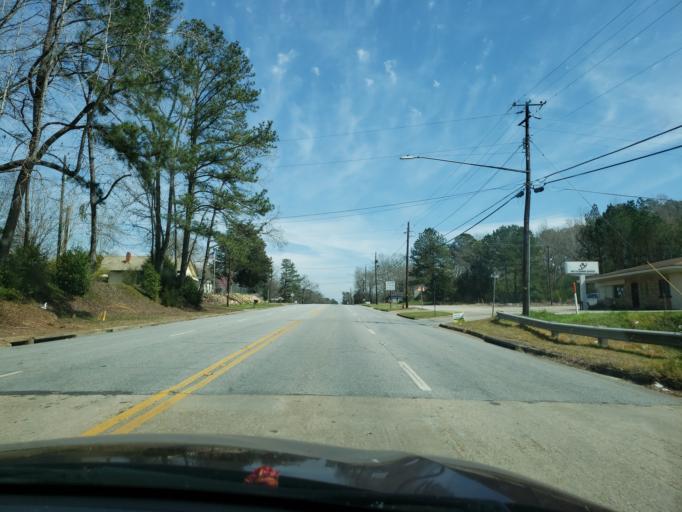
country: US
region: Alabama
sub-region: Elmore County
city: Tallassee
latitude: 32.5516
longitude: -85.8583
